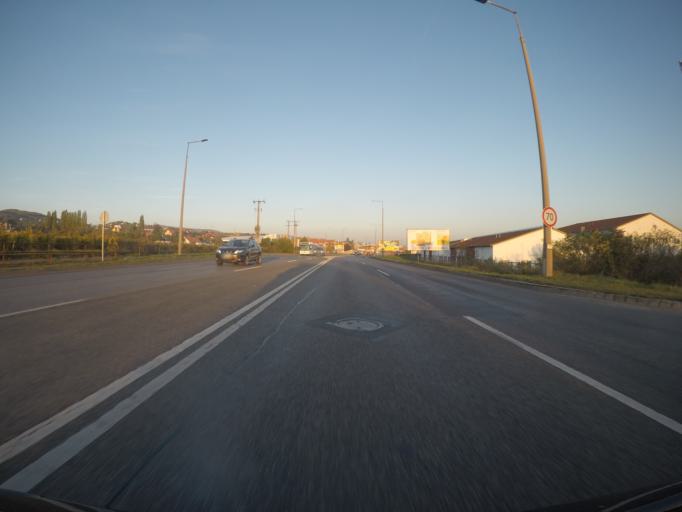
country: HU
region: Baranya
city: Pellerd
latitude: 46.0650
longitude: 18.1611
